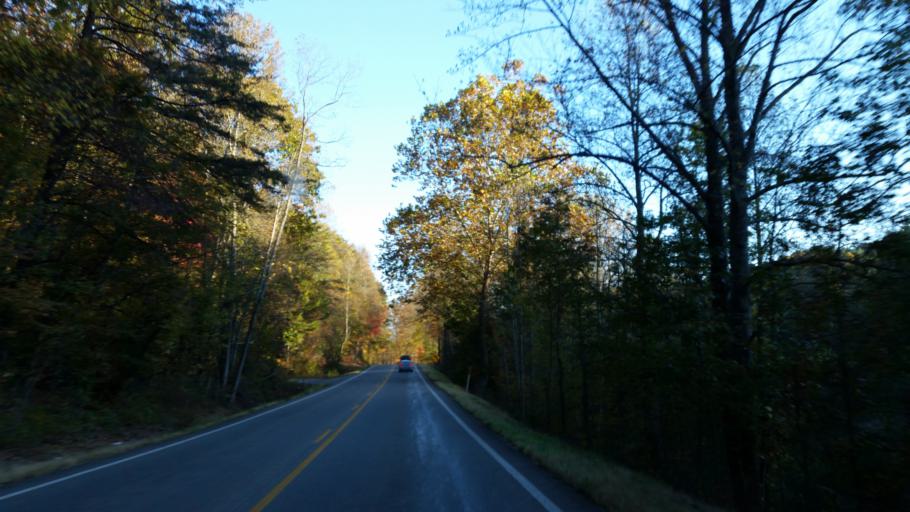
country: US
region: Georgia
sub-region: Pickens County
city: Jasper
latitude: 34.5658
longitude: -84.3080
